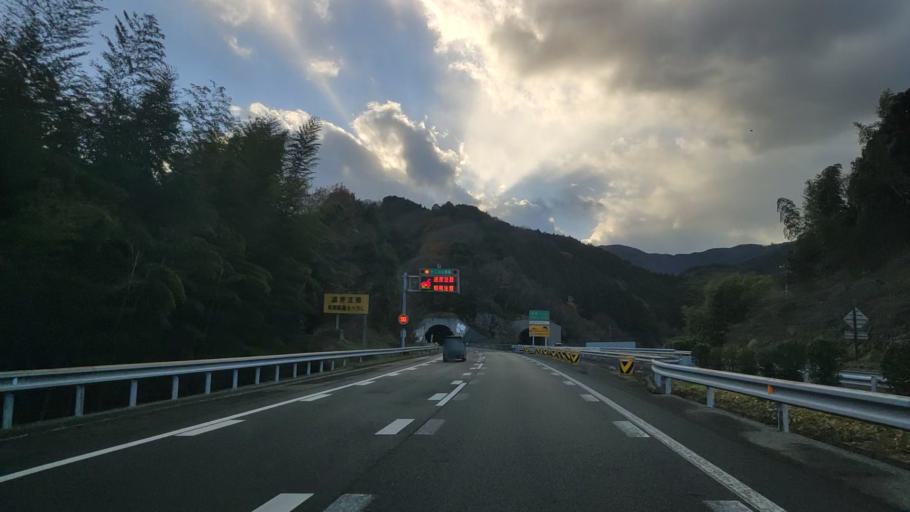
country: JP
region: Ehime
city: Saijo
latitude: 33.8529
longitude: 133.0023
